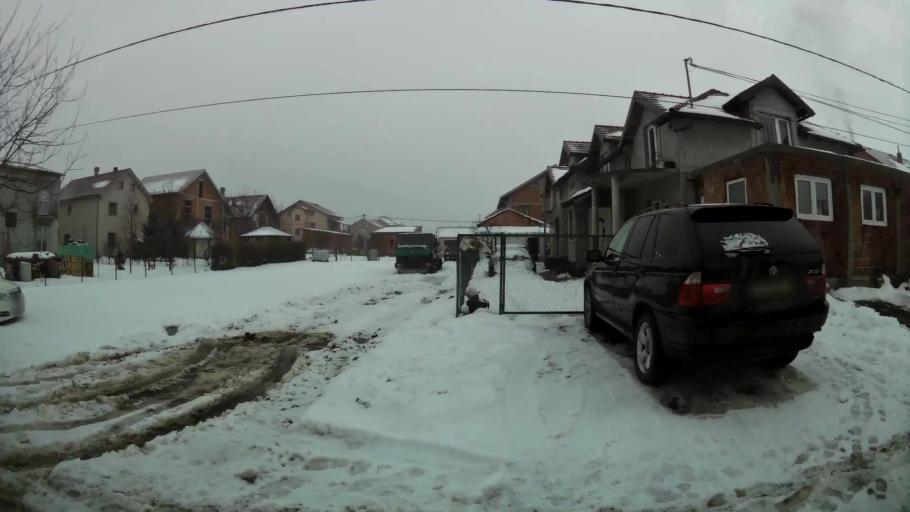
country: RS
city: Novi Banovci
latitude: 44.8759
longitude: 20.3115
